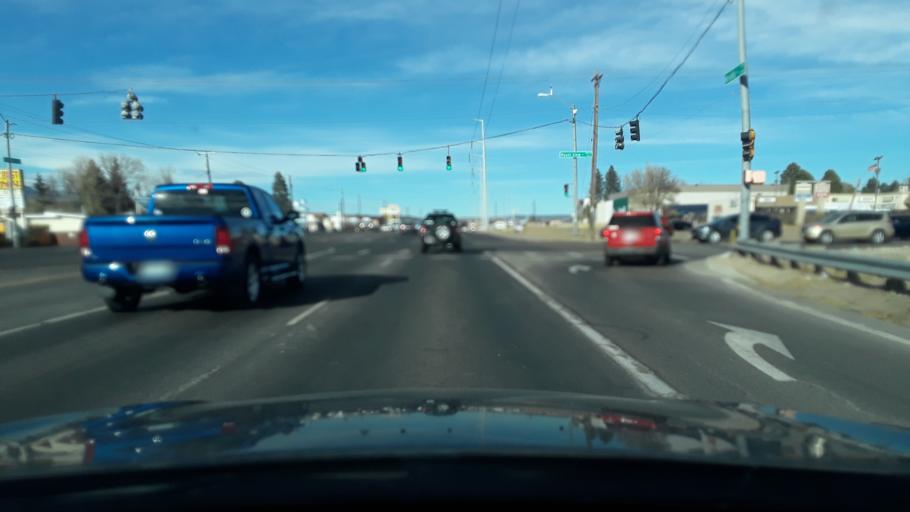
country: US
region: Colorado
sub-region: El Paso County
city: Colorado Springs
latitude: 38.8891
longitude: -104.8184
